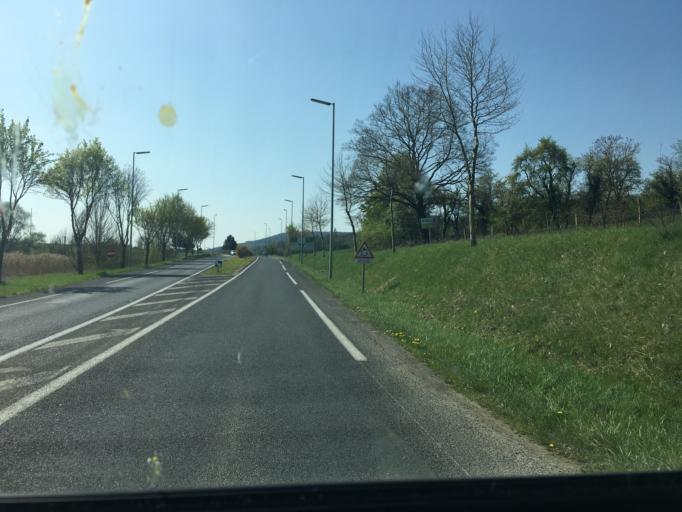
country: FR
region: Lorraine
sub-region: Departement de Meurthe-et-Moselle
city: Norroy-les-Pont-a-Mousson
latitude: 48.9192
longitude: 6.0379
